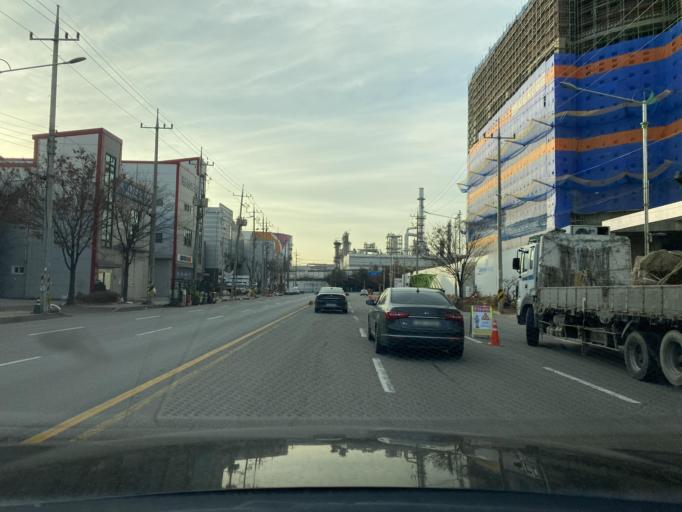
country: KR
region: Incheon
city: Incheon
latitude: 37.5068
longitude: 126.6642
